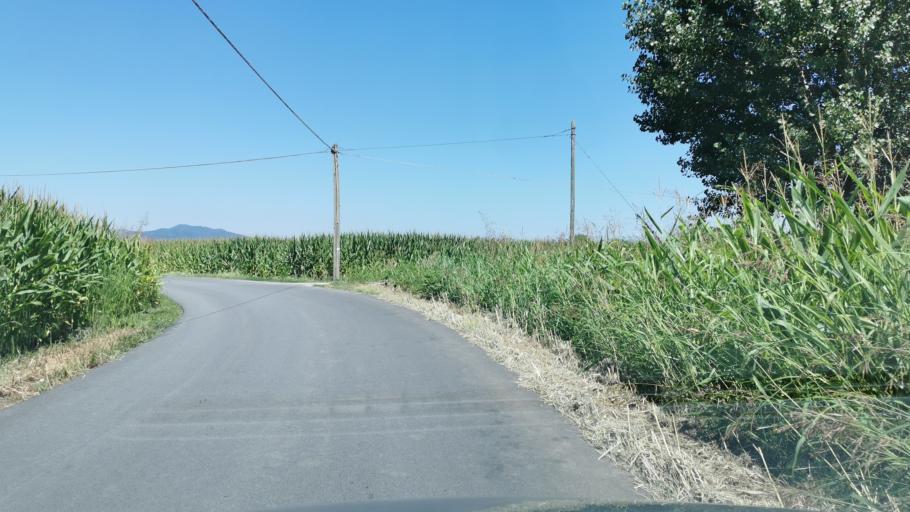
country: IT
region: Piedmont
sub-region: Provincia di Cuneo
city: Caraglio
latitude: 44.4273
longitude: 7.4350
